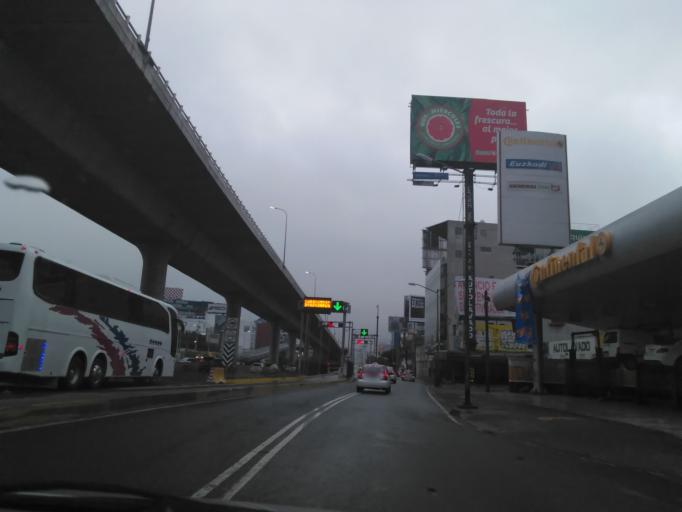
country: MX
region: Mexico City
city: Tlalpan
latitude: 19.3031
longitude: -99.1773
